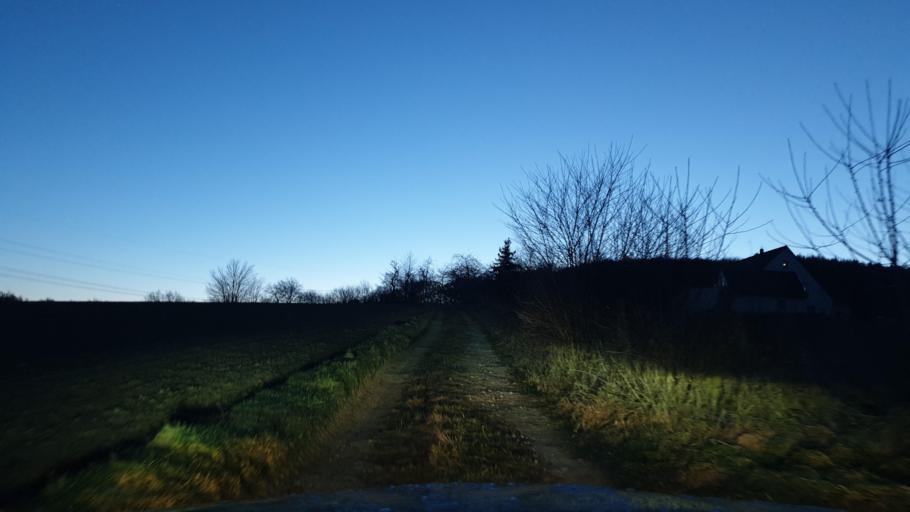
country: DE
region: North Rhine-Westphalia
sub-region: Regierungsbezirk Detmold
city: Hille
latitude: 52.2791
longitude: 8.7570
